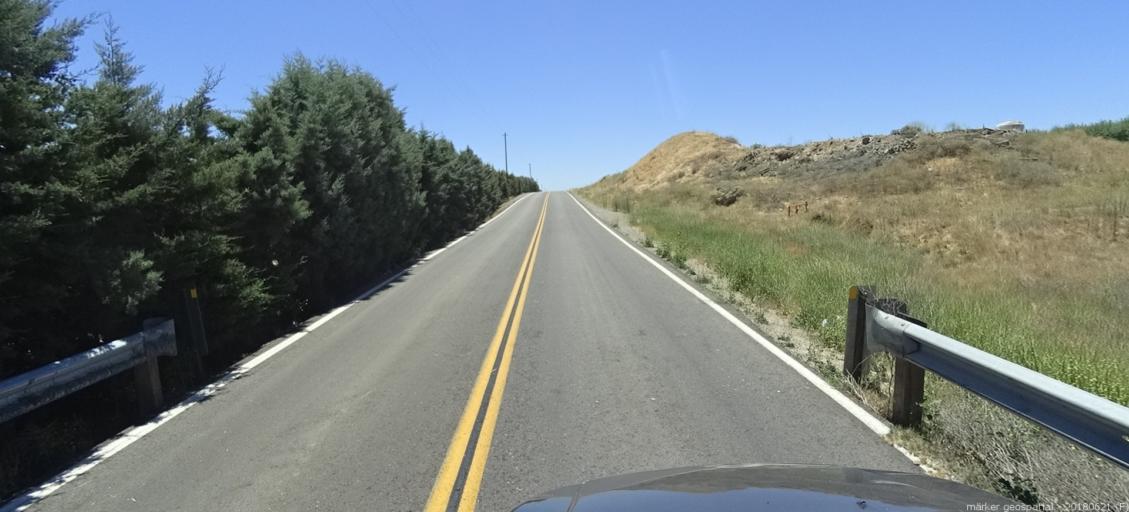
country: US
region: California
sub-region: Madera County
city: Bonadelle Ranchos-Madera Ranchos
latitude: 36.9054
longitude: -119.8940
